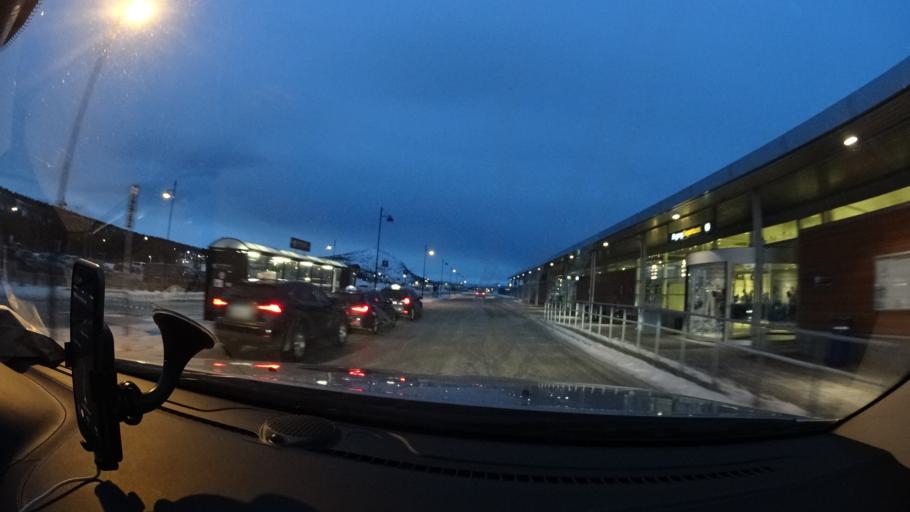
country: NO
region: Finnmark Fylke
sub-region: Alta
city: Alta
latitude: 69.9776
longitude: 23.3468
